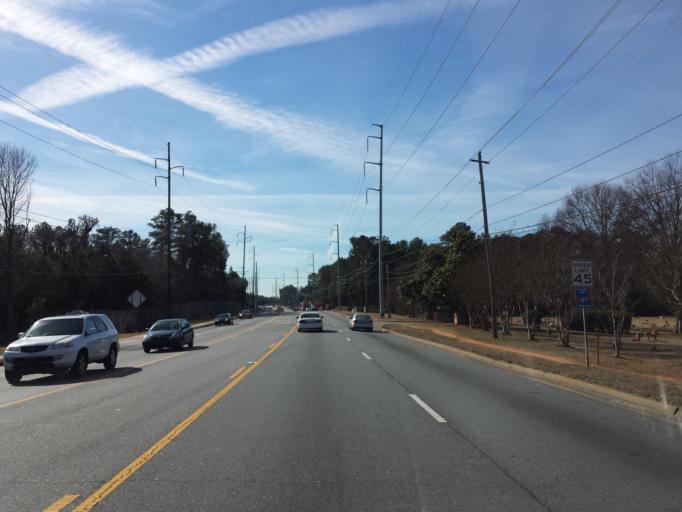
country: US
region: Georgia
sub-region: Cobb County
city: Smyrna
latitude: 33.9012
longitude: -84.4907
